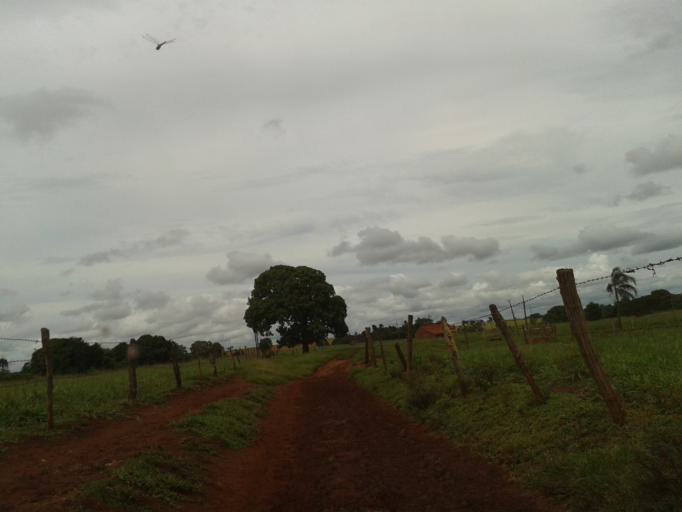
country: BR
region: Minas Gerais
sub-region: Capinopolis
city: Capinopolis
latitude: -18.7780
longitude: -49.7791
